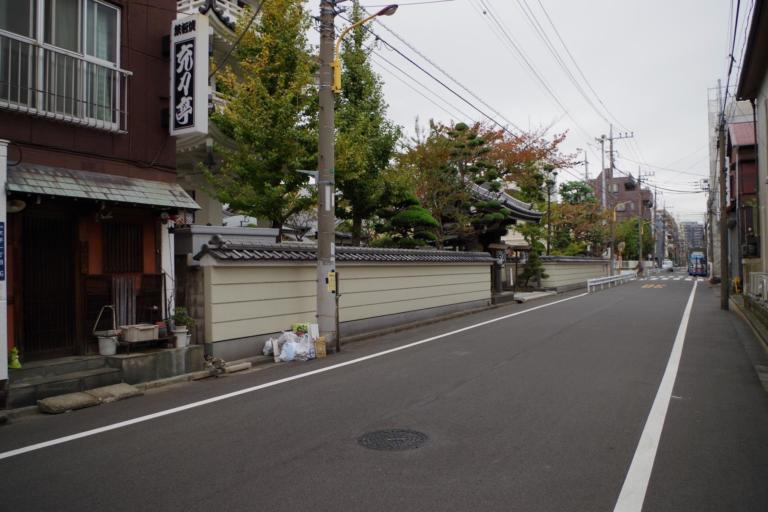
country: JP
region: Tokyo
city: Urayasu
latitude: 35.7019
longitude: 139.8101
